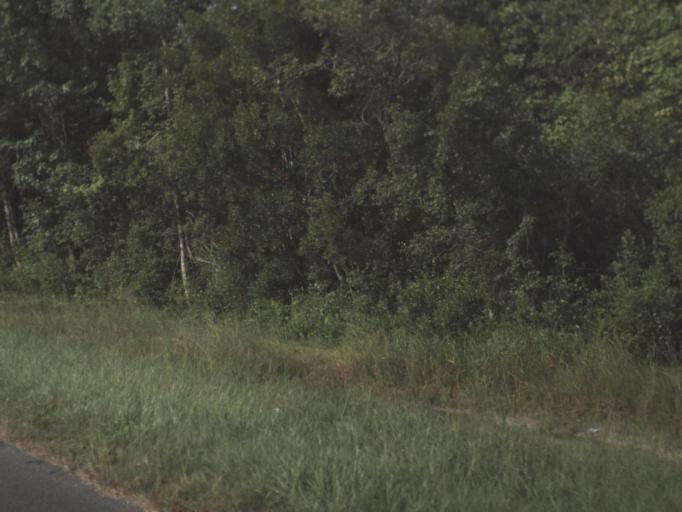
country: US
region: Florida
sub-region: Taylor County
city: Perry
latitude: 30.2421
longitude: -83.6203
